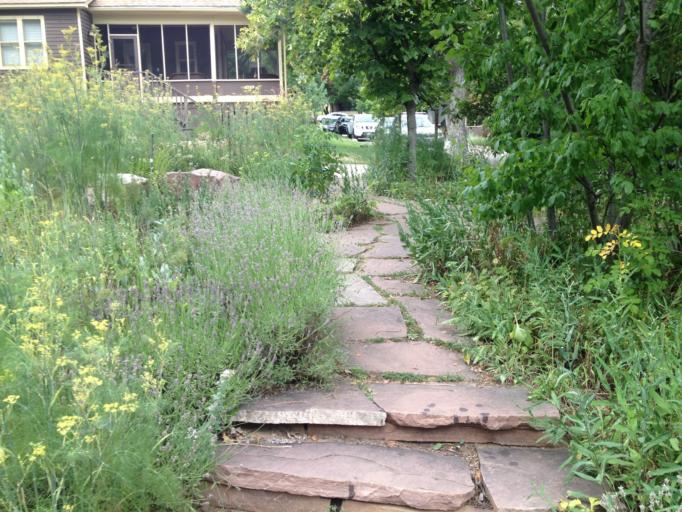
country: US
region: Colorado
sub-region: Boulder County
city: Boulder
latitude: 39.9968
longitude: -105.2811
